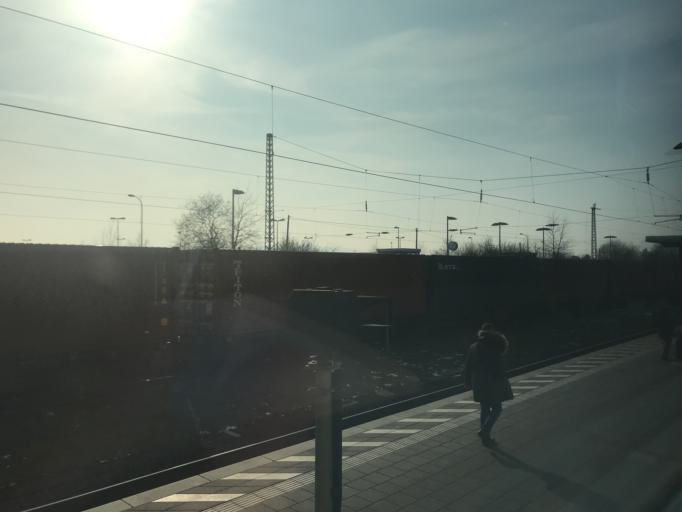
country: DE
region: Rheinland-Pfalz
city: Neuerburg
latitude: 49.9729
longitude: 6.9440
